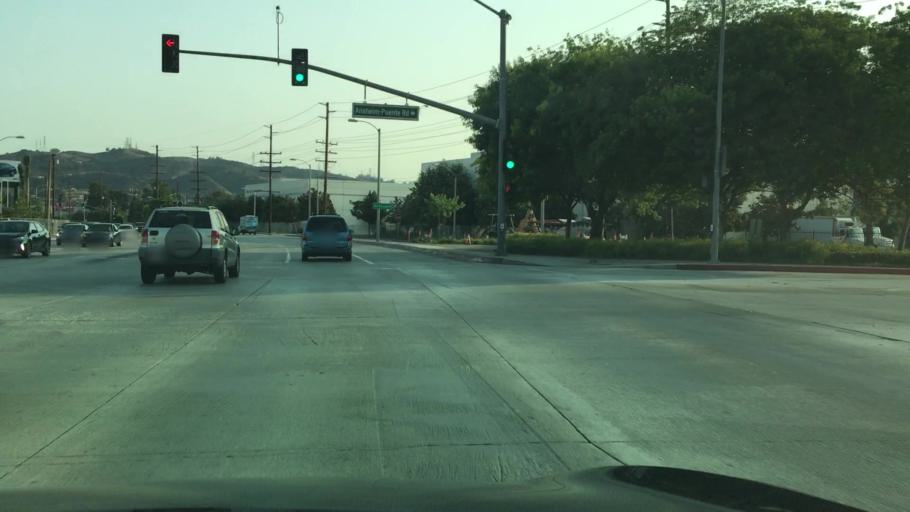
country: US
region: California
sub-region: Los Angeles County
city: La Puente
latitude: 34.0061
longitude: -117.9296
